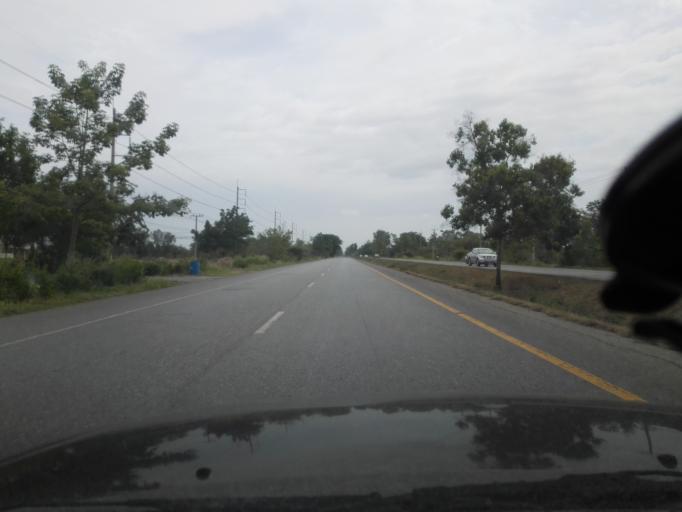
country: TH
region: Kamphaeng Phet
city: Khlong Khlung
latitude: 16.1117
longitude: 99.7191
